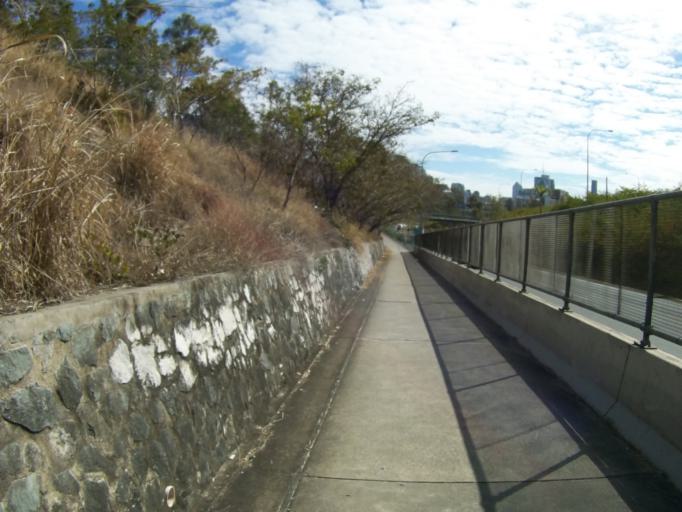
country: AU
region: Queensland
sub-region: Brisbane
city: Woolloongabba
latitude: -27.4875
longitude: 153.0321
